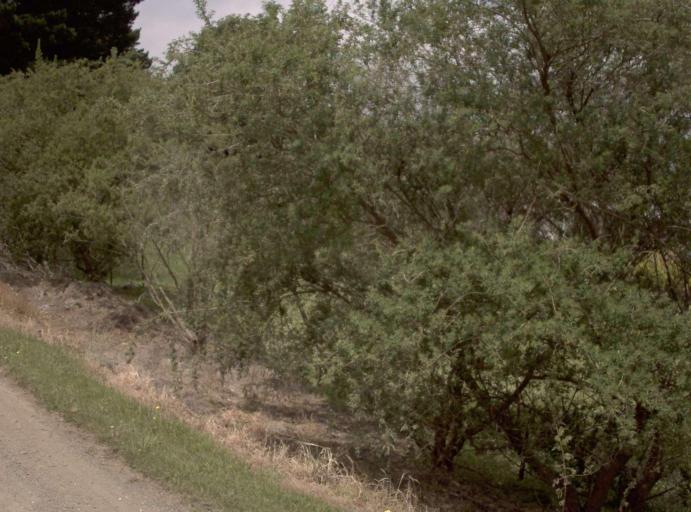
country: AU
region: Victoria
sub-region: Latrobe
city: Traralgon
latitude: -38.4031
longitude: 146.6465
